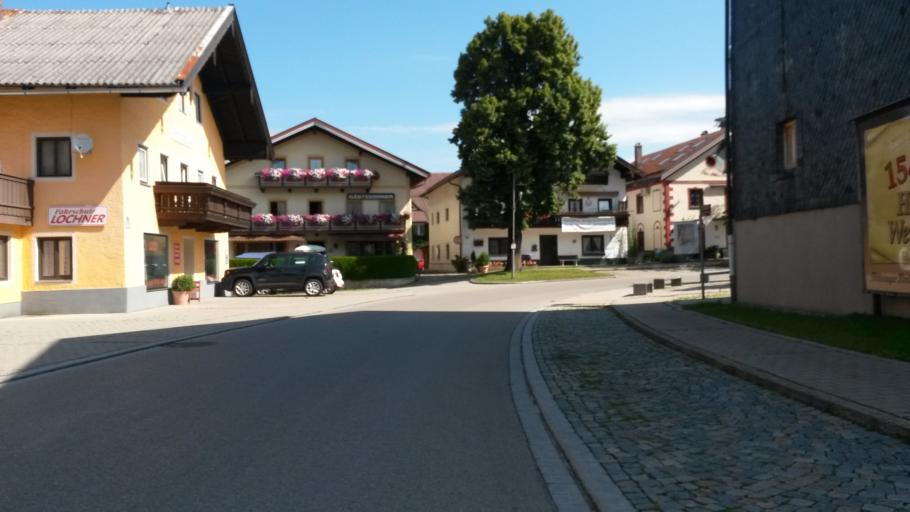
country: DE
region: Bavaria
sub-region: Upper Bavaria
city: Grabenstatt
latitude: 47.8433
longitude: 12.5414
